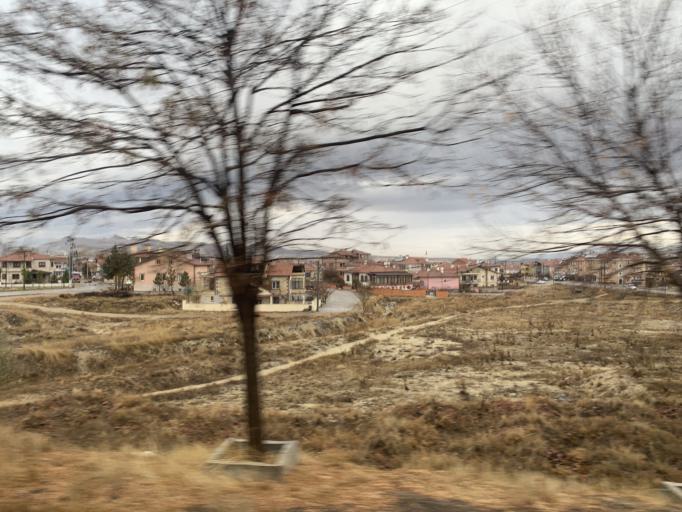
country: TR
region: Nevsehir
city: Avanos
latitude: 38.7111
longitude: 34.8581
